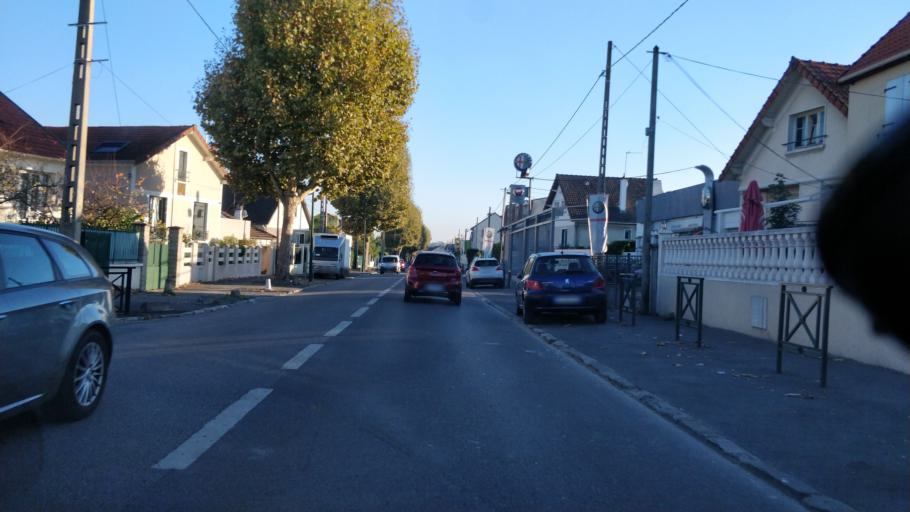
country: FR
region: Ile-de-France
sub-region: Departement de Seine-Saint-Denis
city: Neuilly-sur-Marne
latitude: 48.8723
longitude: 2.5538
